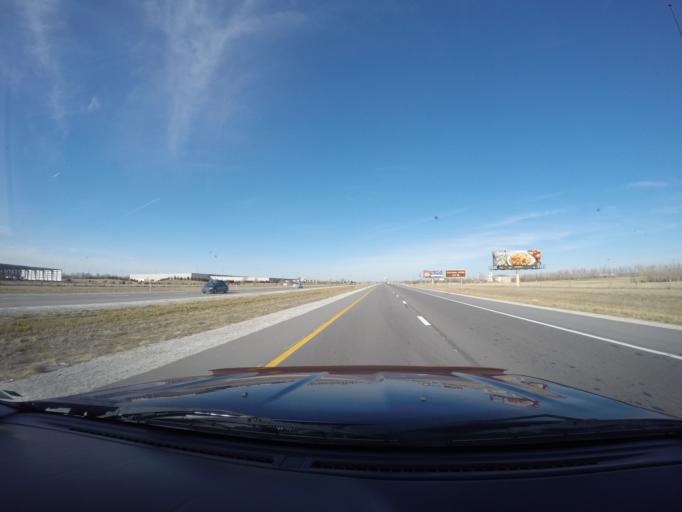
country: US
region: Kansas
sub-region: Sedgwick County
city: Park City
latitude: 37.8163
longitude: -97.3264
